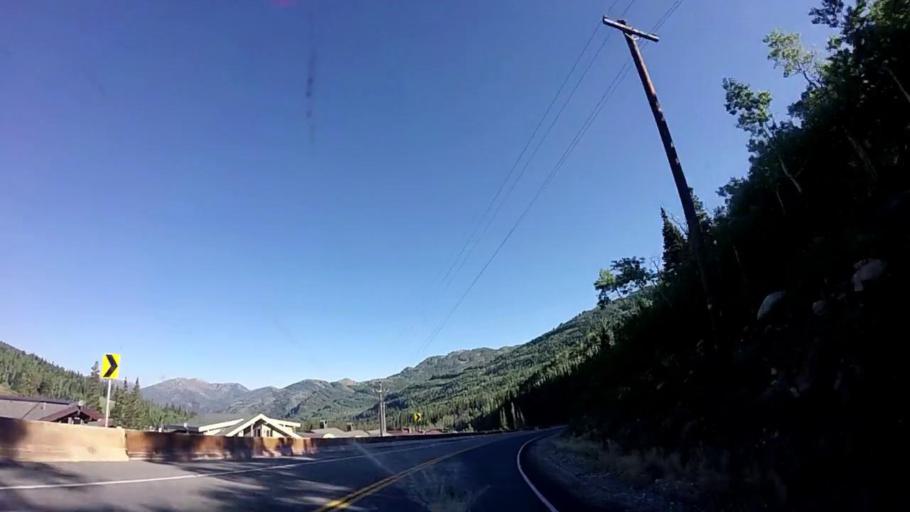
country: US
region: Utah
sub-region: Summit County
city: Snyderville
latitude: 40.6179
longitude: -111.5902
